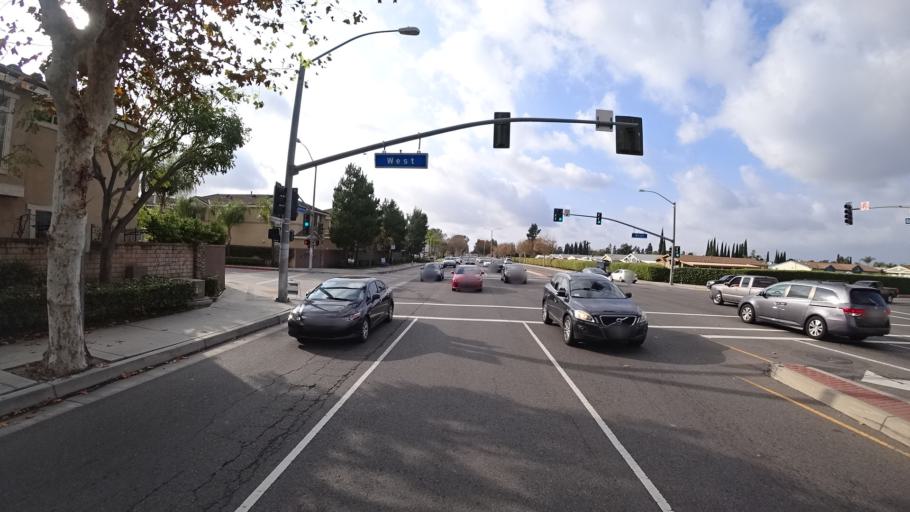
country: US
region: California
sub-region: Orange County
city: Garden Grove
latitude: 33.7743
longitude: -117.9233
